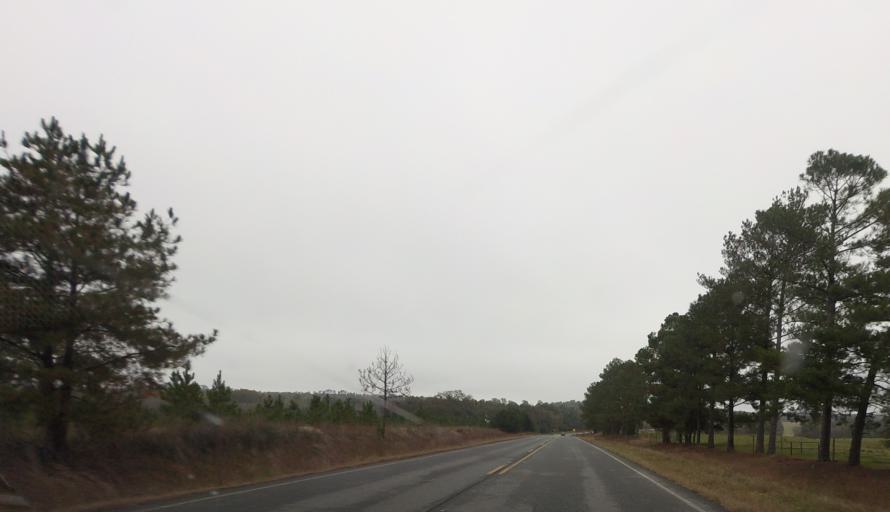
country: US
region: Georgia
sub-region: Marion County
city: Buena Vista
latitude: 32.3689
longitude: -84.4575
